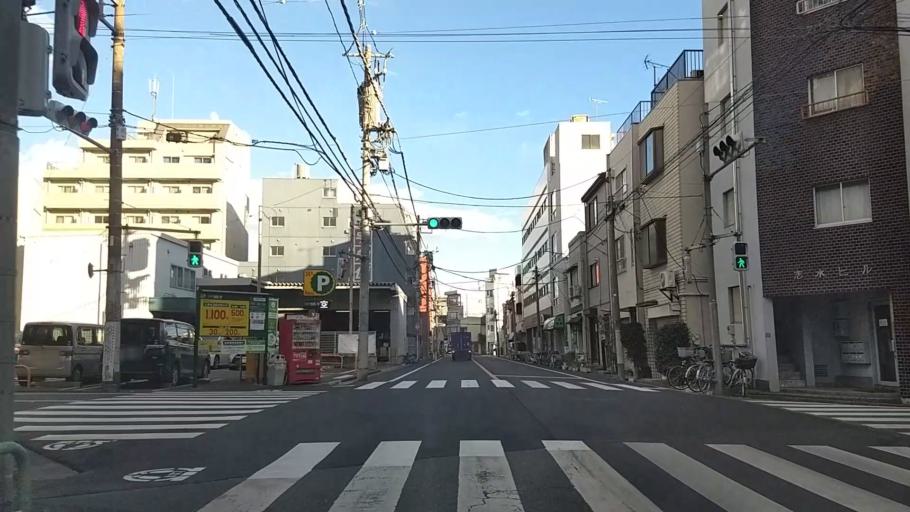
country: JP
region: Saitama
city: Kawaguchi
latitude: 35.7475
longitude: 139.7124
